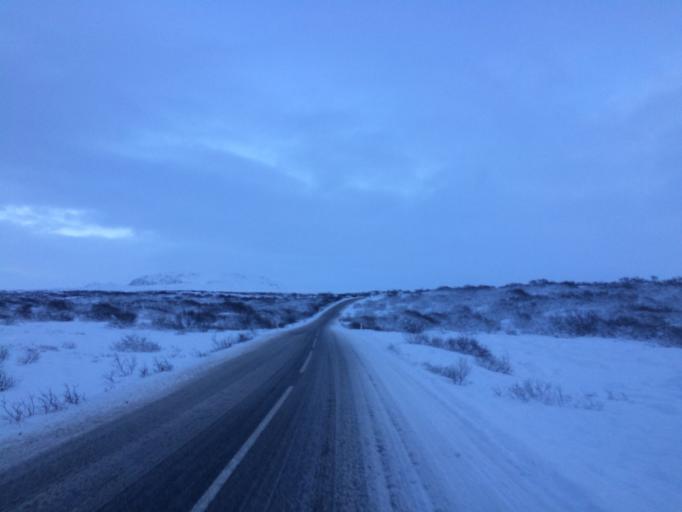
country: IS
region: South
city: Hveragerdi
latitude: 64.2313
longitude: -21.0422
